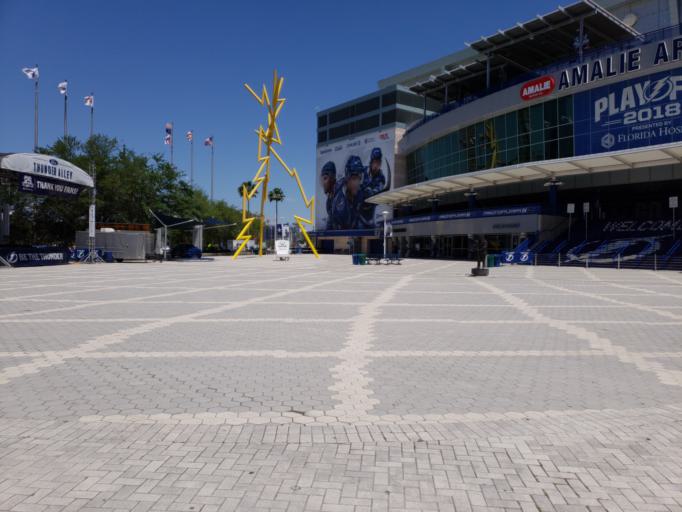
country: US
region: Florida
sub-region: Hillsborough County
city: Tampa
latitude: 27.9425
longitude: -82.4530
